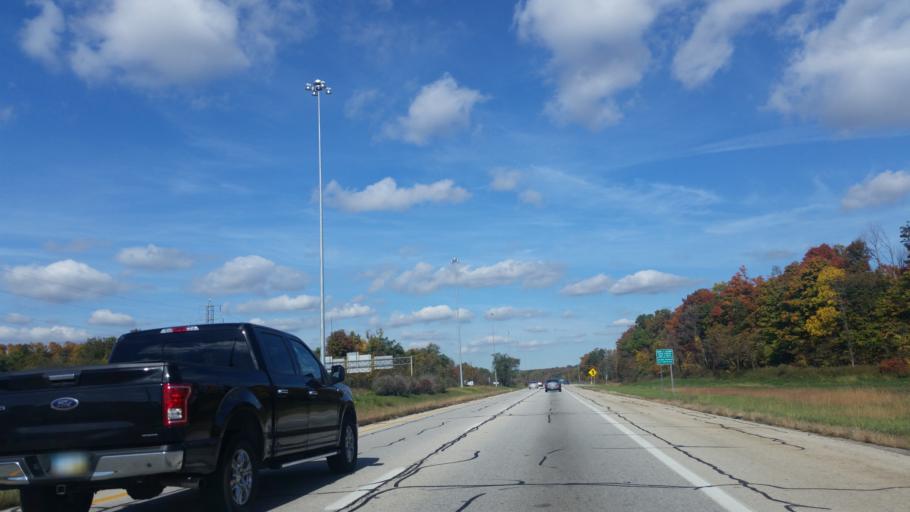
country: US
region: Ohio
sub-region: Summit County
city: Richfield
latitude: 41.2318
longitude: -81.6275
